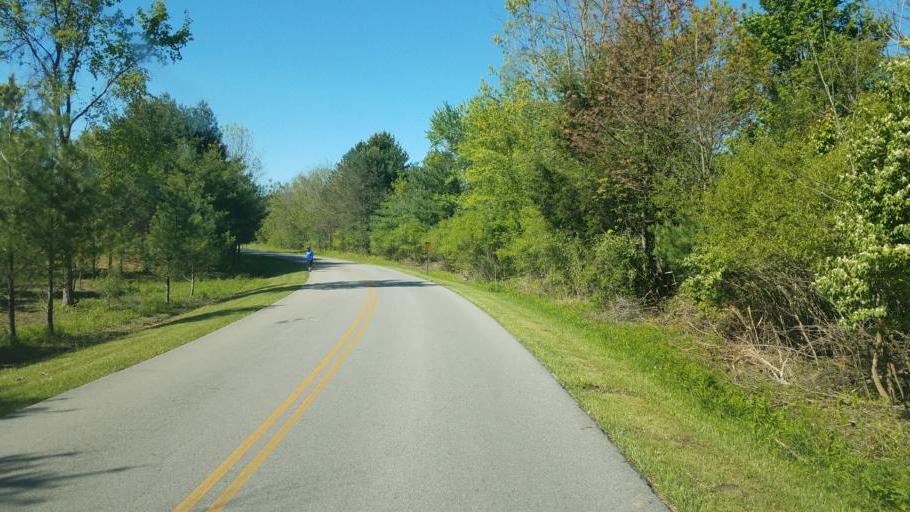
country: US
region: Ohio
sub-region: Delaware County
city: Lewis Center
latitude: 40.2011
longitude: -82.9482
